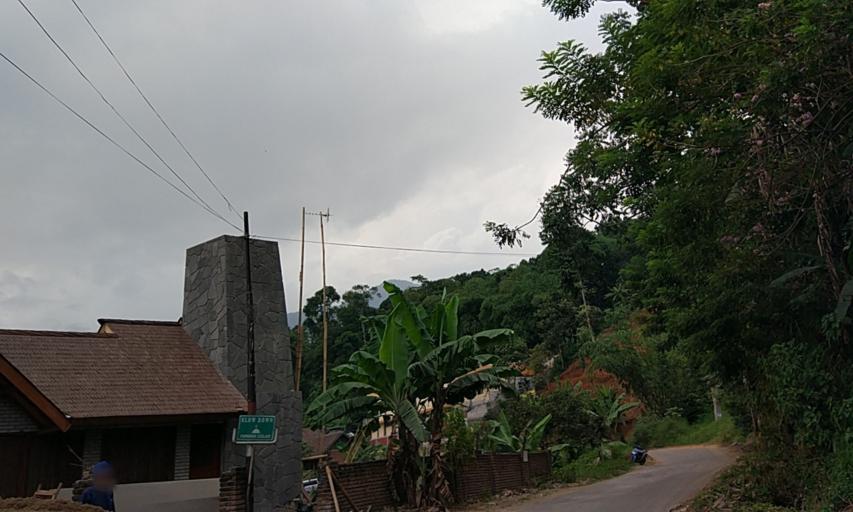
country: ID
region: West Java
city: Bandung
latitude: -6.8792
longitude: 107.6928
